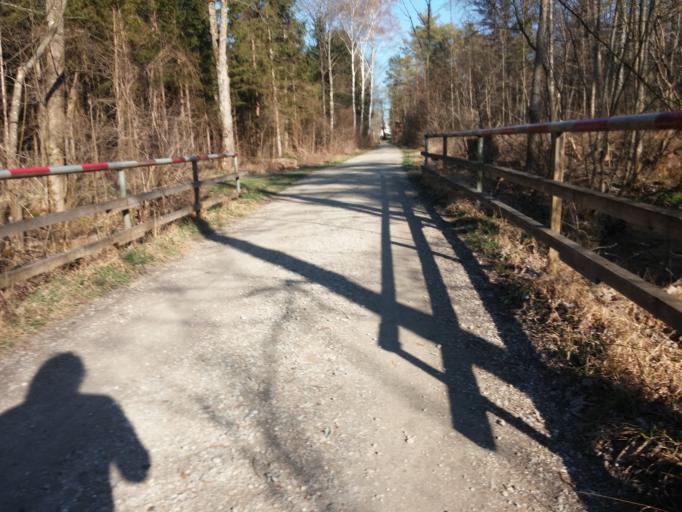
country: DE
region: Bavaria
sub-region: Upper Bavaria
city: Ismaning
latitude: 48.2547
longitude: 11.6902
